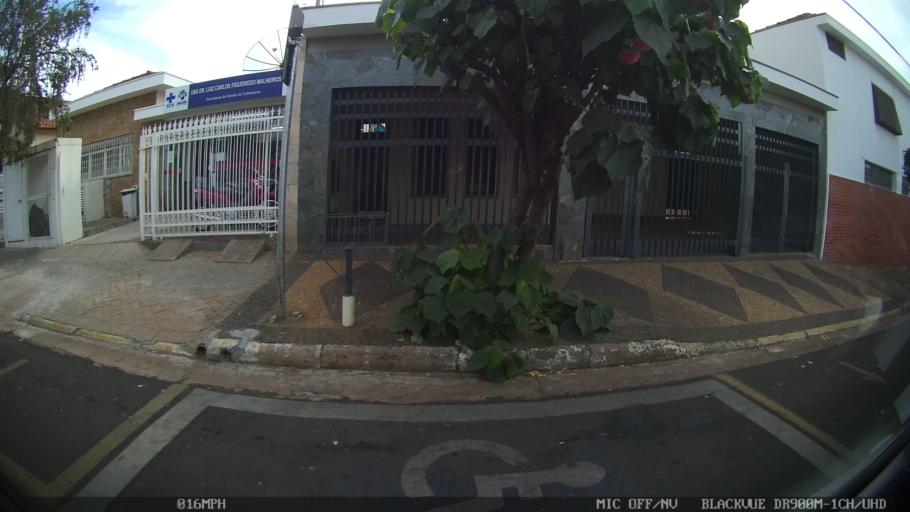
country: BR
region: Sao Paulo
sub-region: Catanduva
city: Catanduva
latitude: -21.1381
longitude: -48.9776
